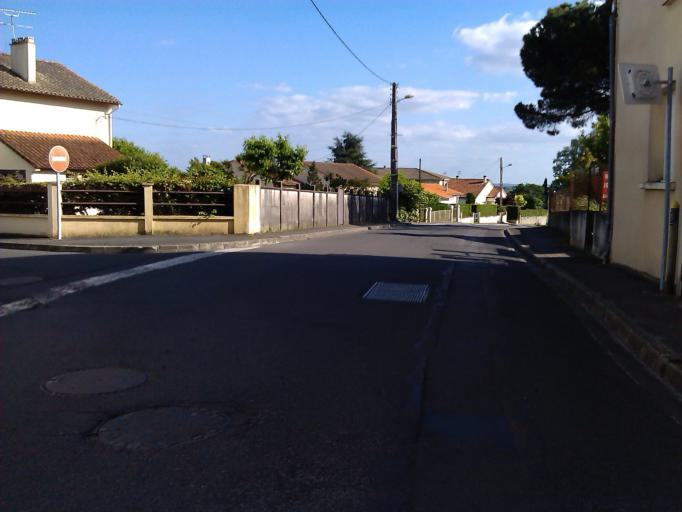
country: FR
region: Aquitaine
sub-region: Departement de la Gironde
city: Saint-Gervais
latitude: 44.9966
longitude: -0.4486
